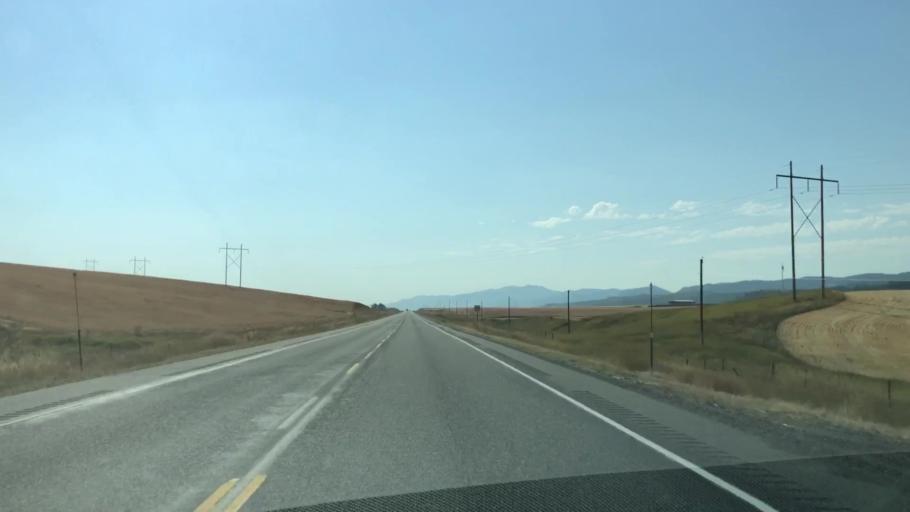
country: US
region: Idaho
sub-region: Teton County
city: Victor
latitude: 43.5241
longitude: -111.4960
